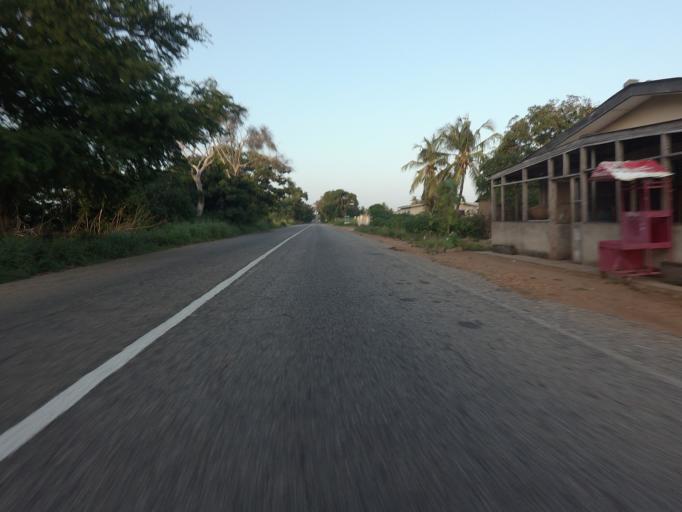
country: GH
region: Volta
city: Anloga
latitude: 5.7908
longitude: 0.8732
